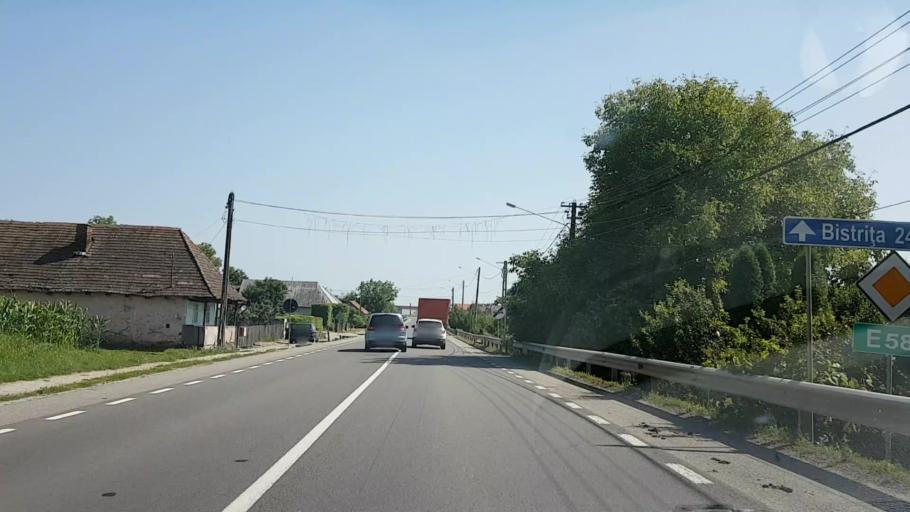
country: RO
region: Bistrita-Nasaud
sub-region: Comuna Sieu-Odorhei
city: Sieu-Odorhei
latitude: 47.1398
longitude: 24.3067
